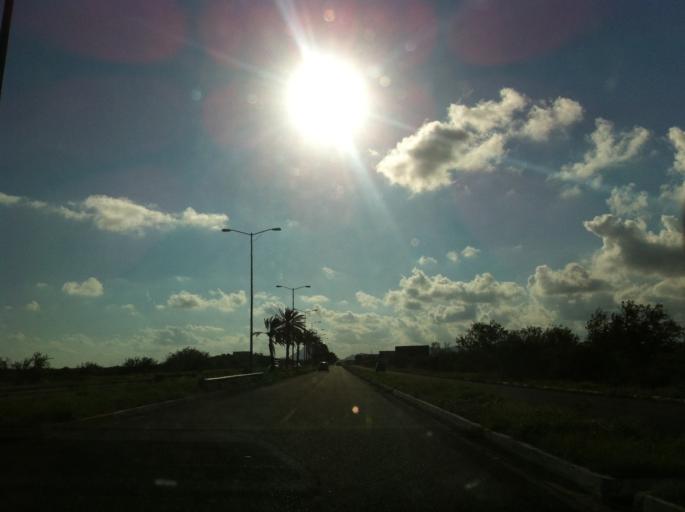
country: MX
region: Sonora
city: Heroica Guaymas
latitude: 27.9776
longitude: -110.9754
